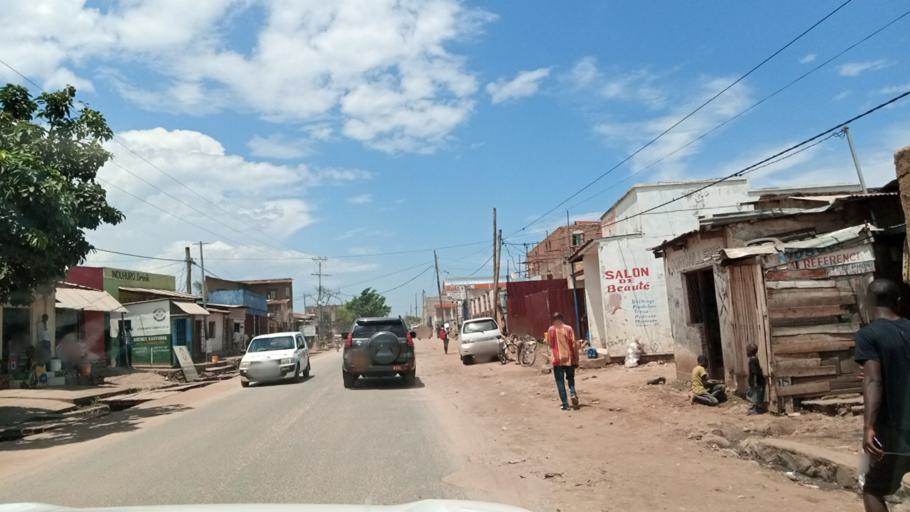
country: BI
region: Bujumbura Mairie
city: Bujumbura
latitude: -3.4253
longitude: 29.3557
